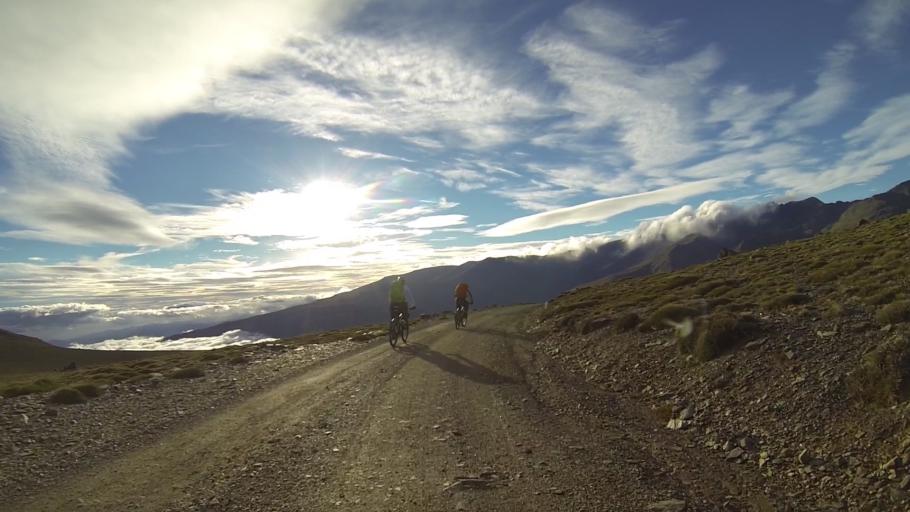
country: ES
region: Andalusia
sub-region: Provincia de Granada
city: Trevelez
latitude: 37.0028
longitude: -3.3089
